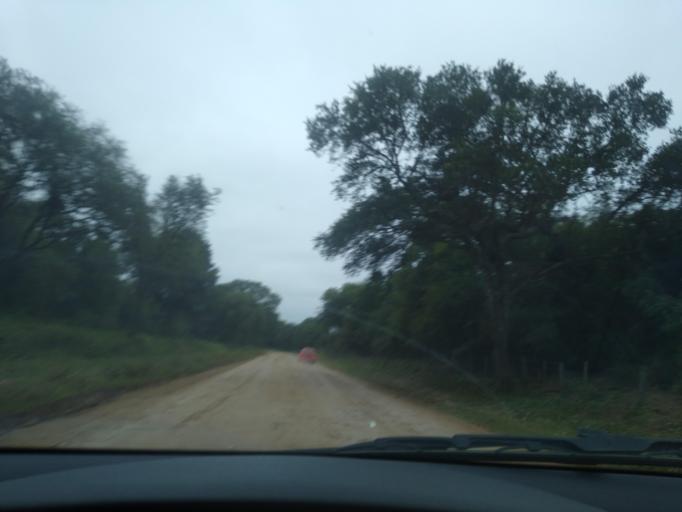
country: AR
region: Chaco
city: Colonia Benitez
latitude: -27.3435
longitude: -58.9697
